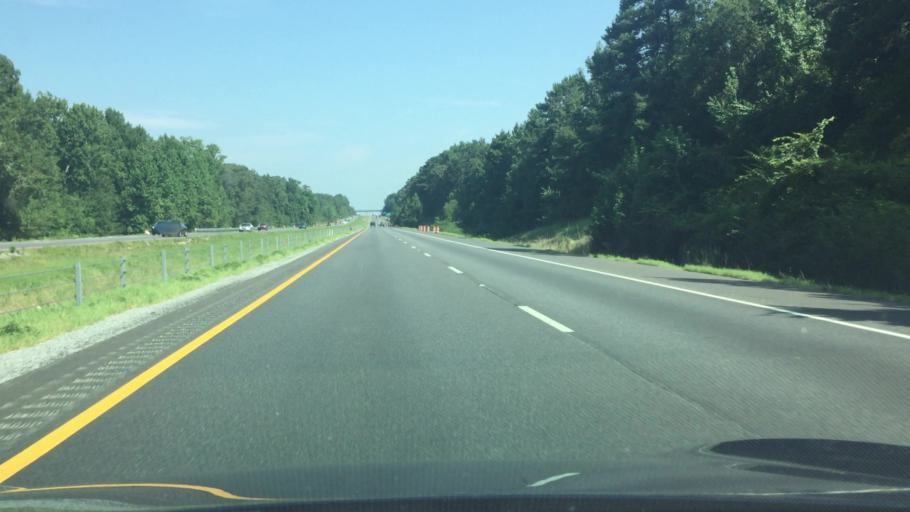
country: US
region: Alabama
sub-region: Chilton County
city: Clanton
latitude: 32.8209
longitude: -86.5870
